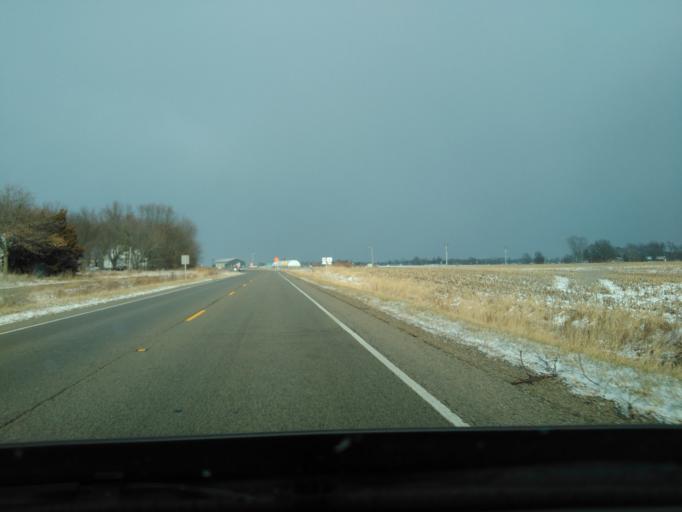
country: US
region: Illinois
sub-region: Madison County
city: Highland
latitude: 38.7782
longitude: -89.6347
